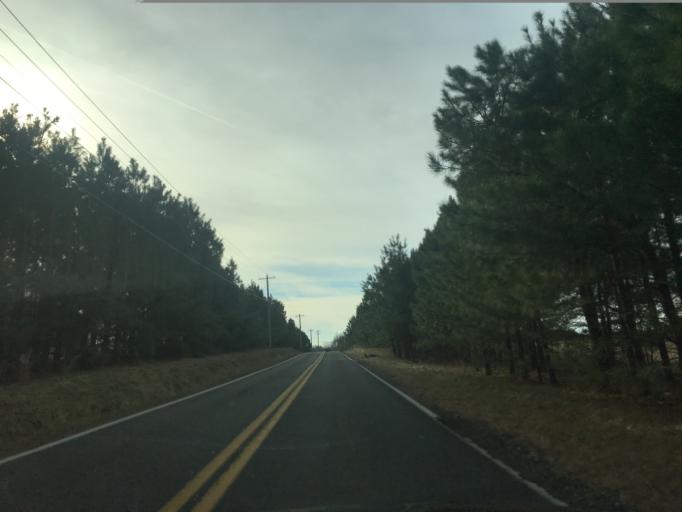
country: US
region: Maryland
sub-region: Charles County
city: Hughesville
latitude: 38.5250
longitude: -76.8423
